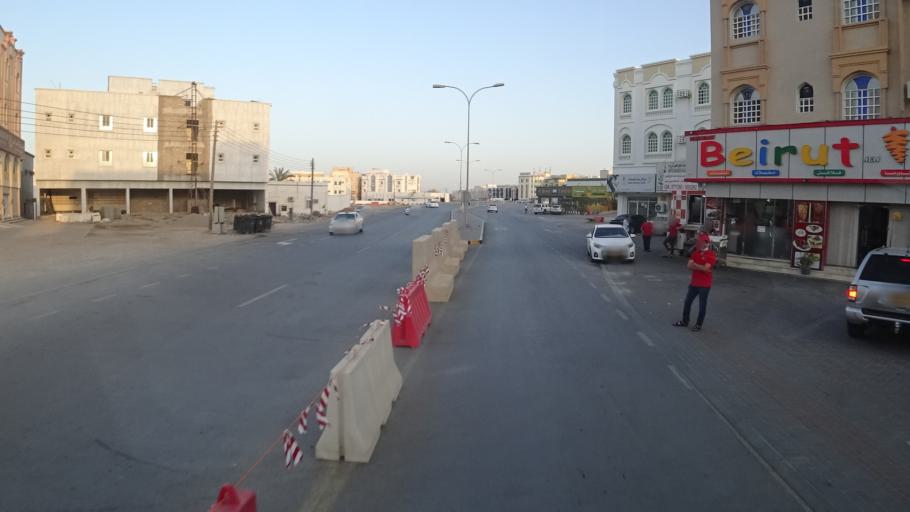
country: OM
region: Ash Sharqiyah
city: Sur
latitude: 22.5796
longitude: 59.5122
